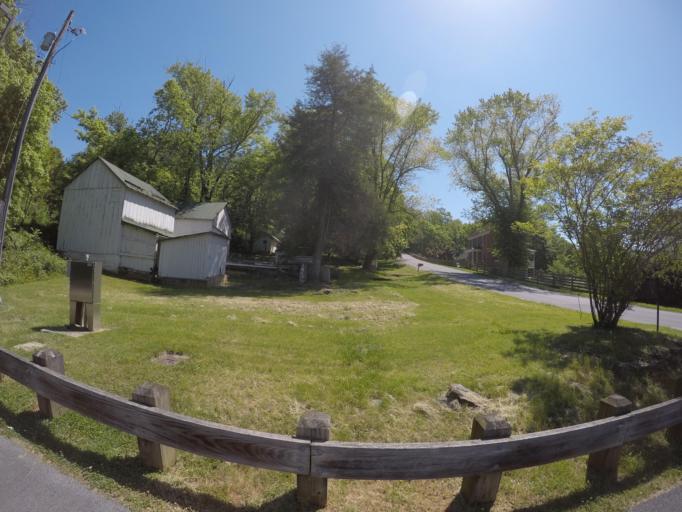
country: US
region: West Virginia
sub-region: Jefferson County
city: Shepherdstown
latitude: 39.4366
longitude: -77.7995
